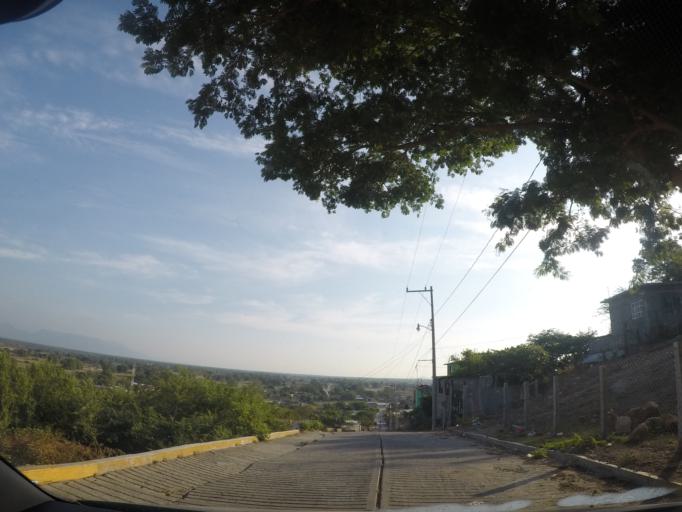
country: MX
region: Oaxaca
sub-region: Santo Domingo Tehuantepec
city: La Noria
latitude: 16.2433
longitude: -95.1504
